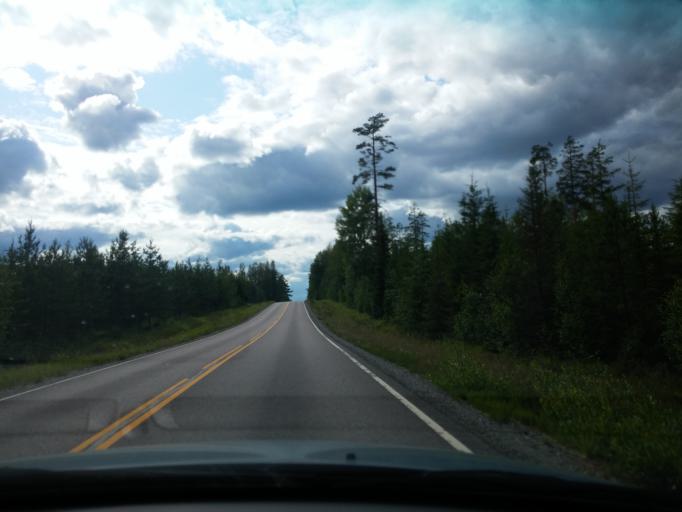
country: FI
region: Central Finland
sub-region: Saarijaervi-Viitasaari
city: Pylkoenmaeki
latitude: 62.6144
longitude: 24.7237
